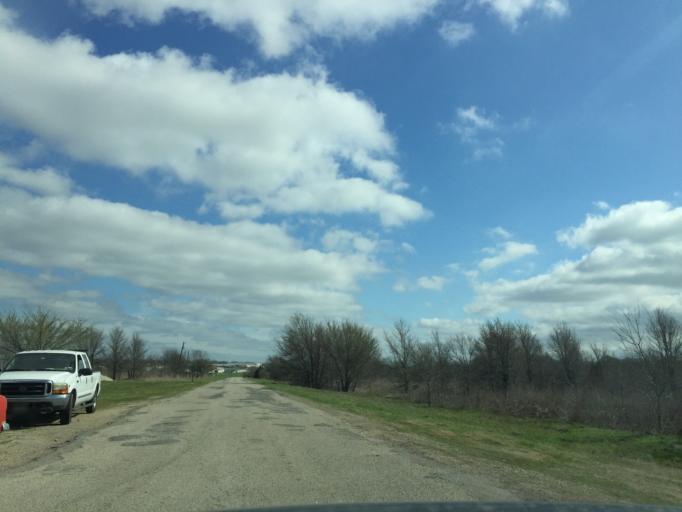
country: US
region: Texas
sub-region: Williamson County
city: Taylor
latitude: 30.5606
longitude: -97.4478
